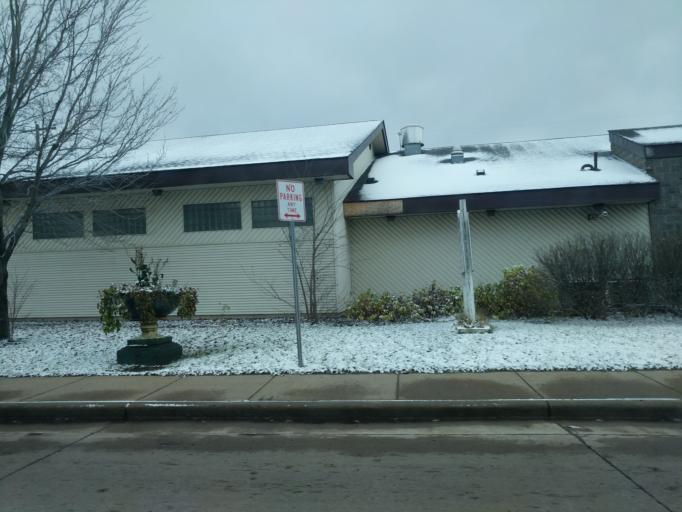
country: US
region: Wisconsin
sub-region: Sawyer County
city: Hayward
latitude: 46.0139
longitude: -91.4833
